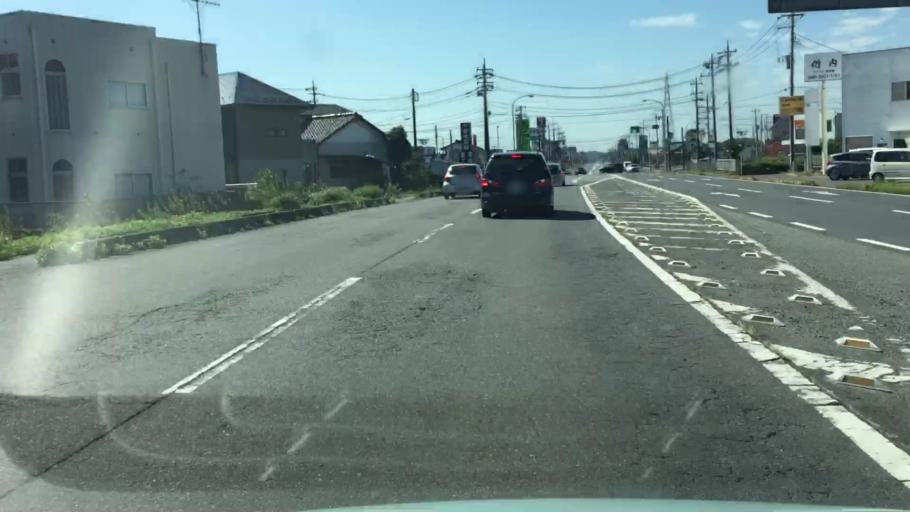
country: JP
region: Ibaraki
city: Ryugasaki
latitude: 35.9092
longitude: 140.1740
